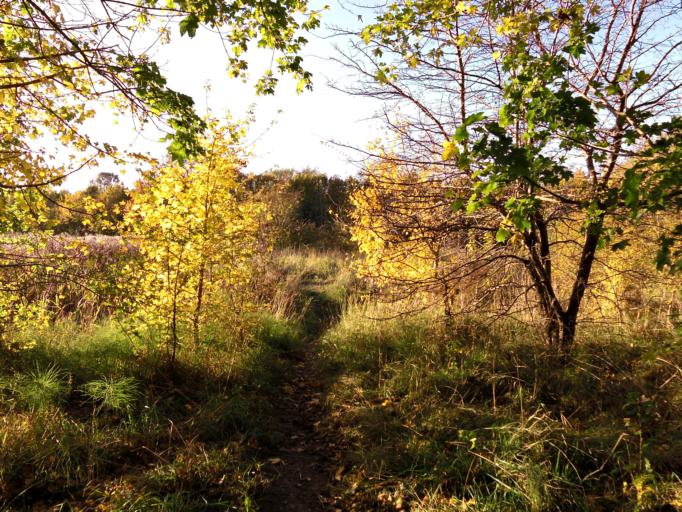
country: DK
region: Central Jutland
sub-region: Arhus Kommune
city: Stavtrup
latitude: 56.1285
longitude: 10.1369
